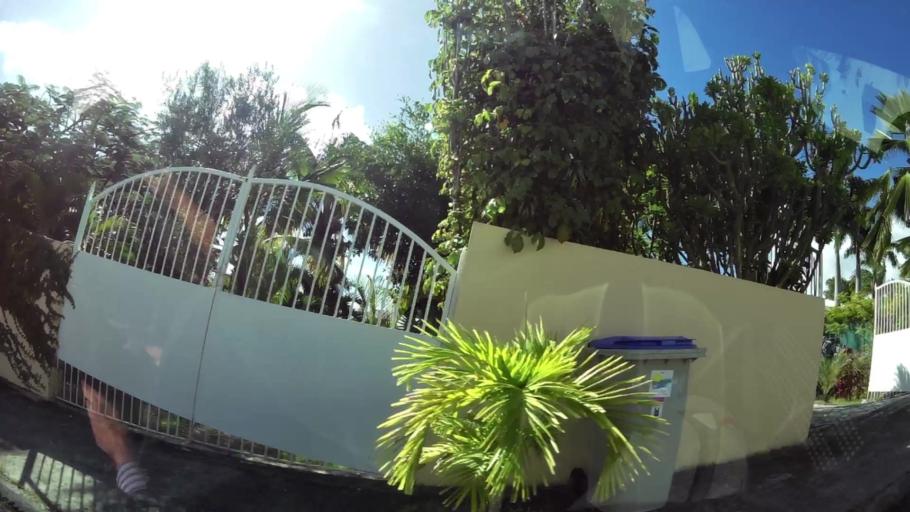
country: GP
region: Guadeloupe
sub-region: Guadeloupe
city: Sainte-Anne
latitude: 16.2366
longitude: -61.3801
